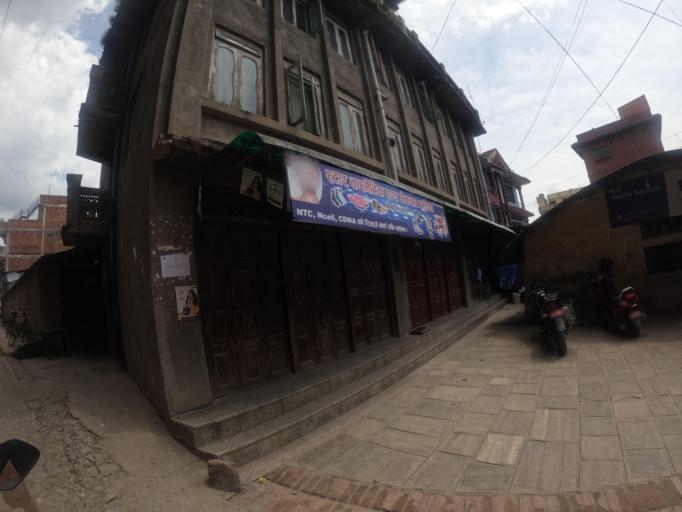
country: NP
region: Central Region
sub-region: Bagmati Zone
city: Bhaktapur
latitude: 27.6839
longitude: 85.3859
